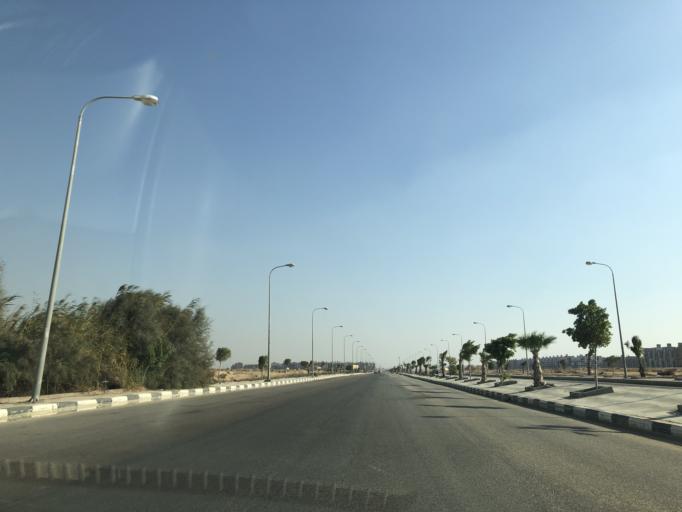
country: EG
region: Al Jizah
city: Madinat Sittah Uktubar
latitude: 29.9161
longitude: 31.0650
